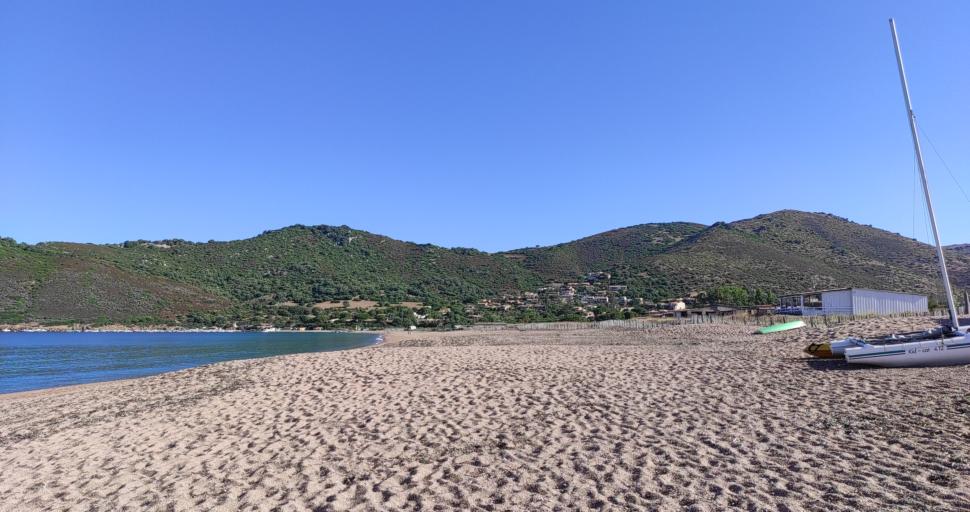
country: FR
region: Corsica
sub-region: Departement de la Corse-du-Sud
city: Alata
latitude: 41.9872
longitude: 8.6703
